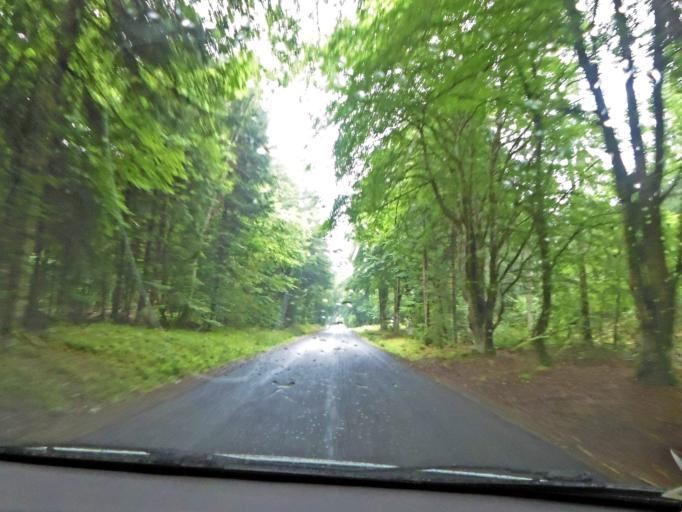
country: FR
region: Auvergne
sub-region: Departement du Puy-de-Dome
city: Orcines
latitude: 45.7440
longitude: 2.9415
